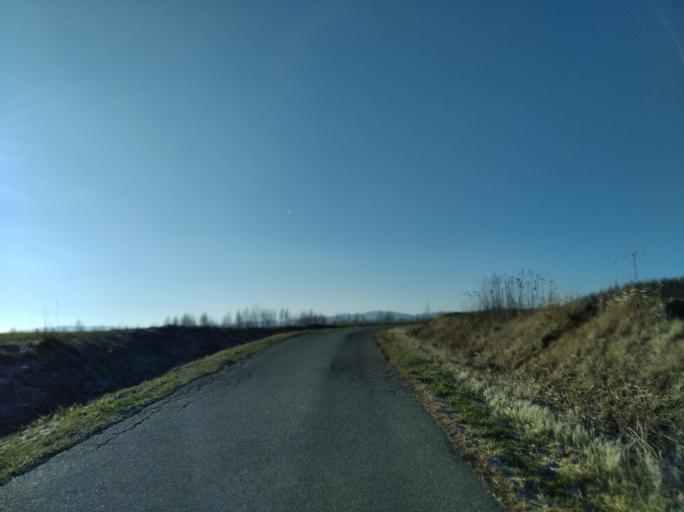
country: PL
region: Subcarpathian Voivodeship
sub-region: Powiat strzyzowski
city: Wysoka Strzyzowska
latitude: 49.8515
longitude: 21.7521
